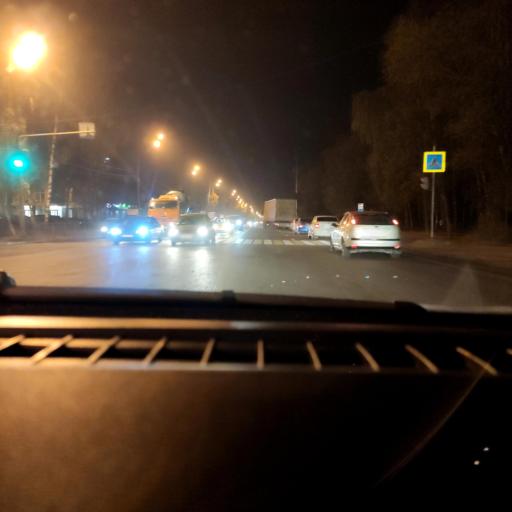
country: RU
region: Voronezj
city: Pridonskoy
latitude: 51.6870
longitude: 39.1102
